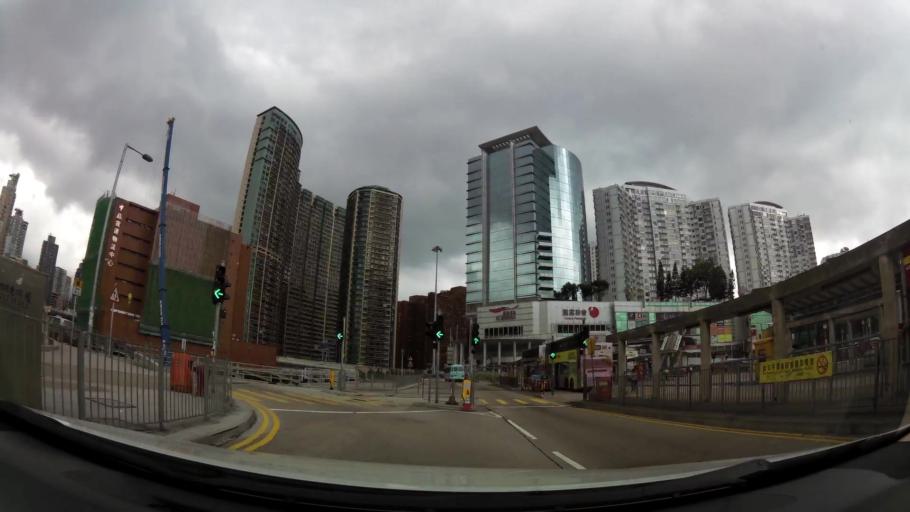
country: HK
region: Kowloon City
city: Kowloon
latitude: 22.3042
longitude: 114.1819
